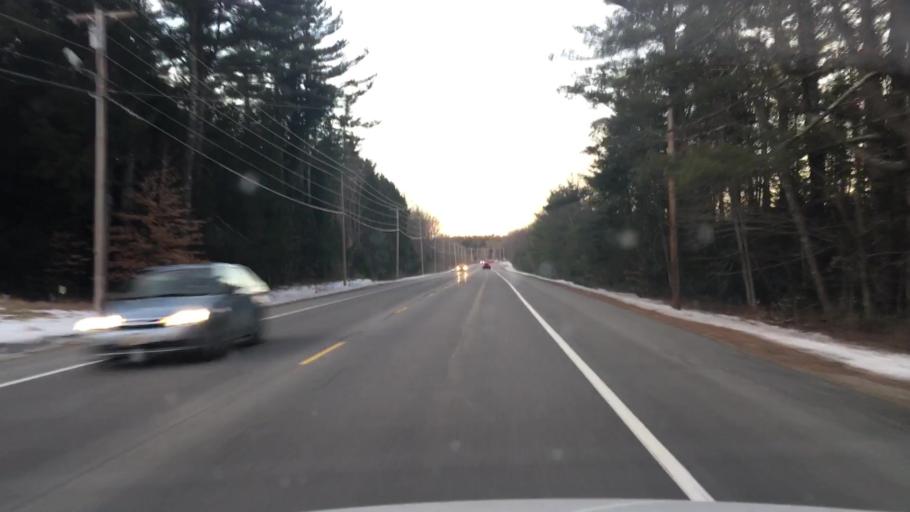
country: US
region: Maine
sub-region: York County
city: Lebanon
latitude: 43.3917
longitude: -70.8765
